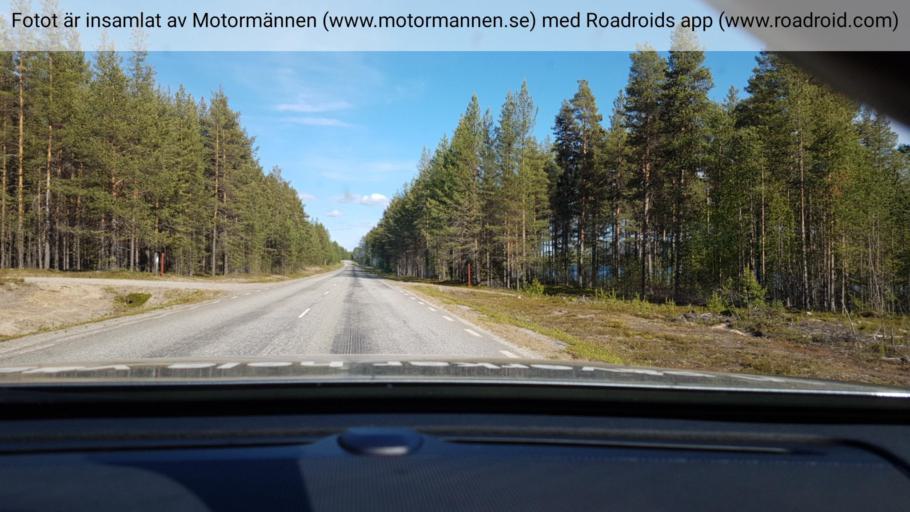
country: SE
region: Vaesterbotten
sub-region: Lycksele Kommun
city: Lycksele
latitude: 64.8228
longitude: 18.8213
